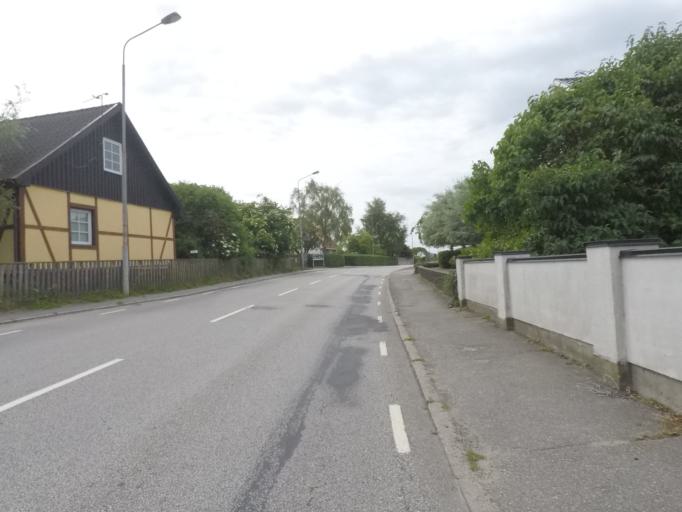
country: SE
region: Skane
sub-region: Malmo
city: Tygelsjo
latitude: 55.5273
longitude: 12.9963
